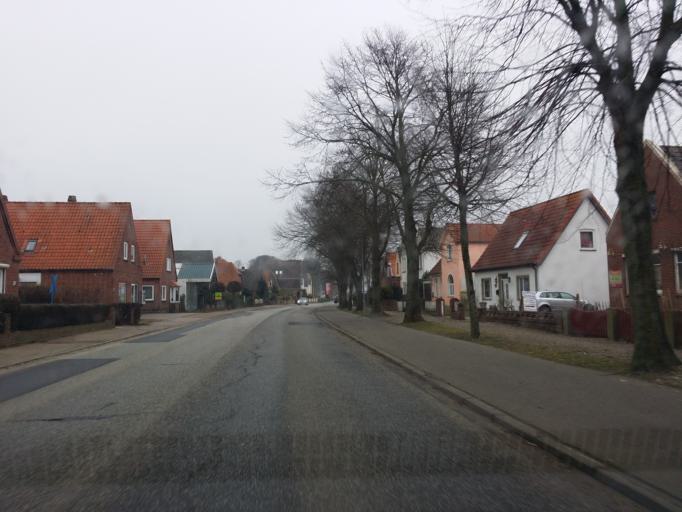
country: DE
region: Schleswig-Holstein
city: Fehmarn
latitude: 54.4423
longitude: 11.1851
